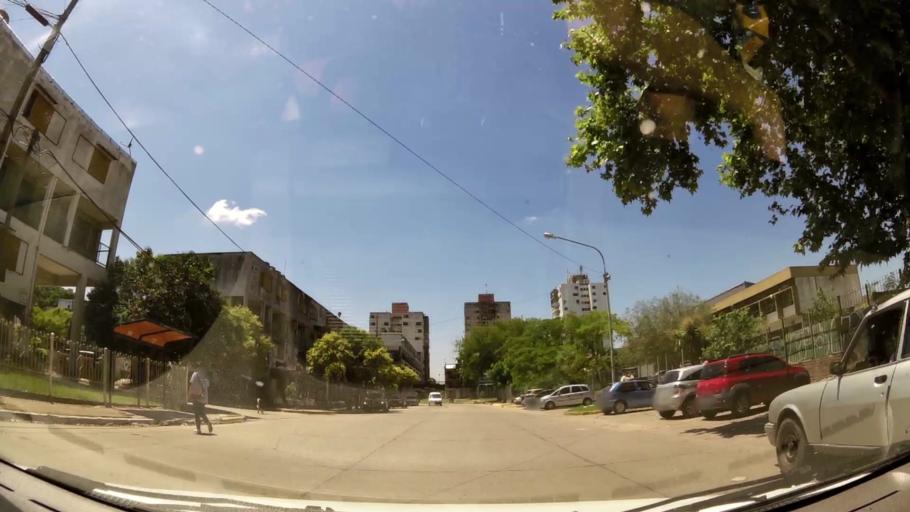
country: AR
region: Buenos Aires
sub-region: Partido de Merlo
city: Merlo
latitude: -34.6530
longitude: -58.7117
